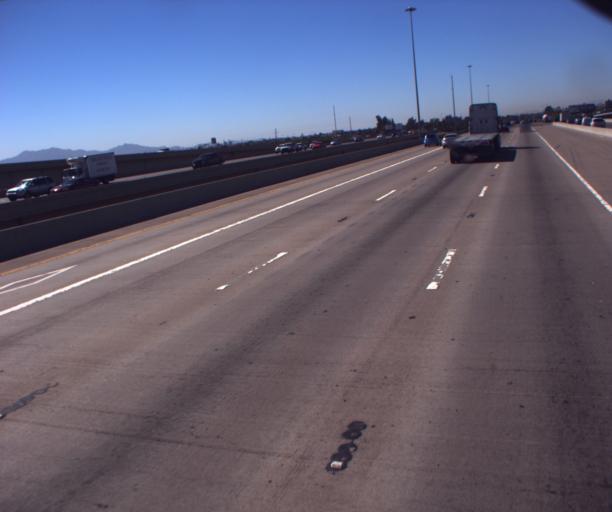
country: US
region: Arizona
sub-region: Maricopa County
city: Phoenix
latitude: 33.4620
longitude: -112.1123
